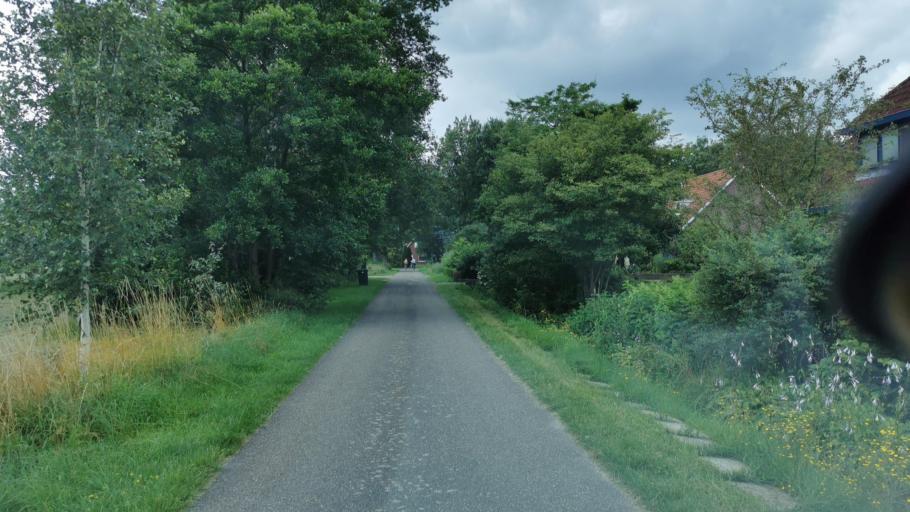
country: NL
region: Overijssel
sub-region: Gemeente Losser
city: Losser
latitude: 52.2466
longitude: 7.0010
